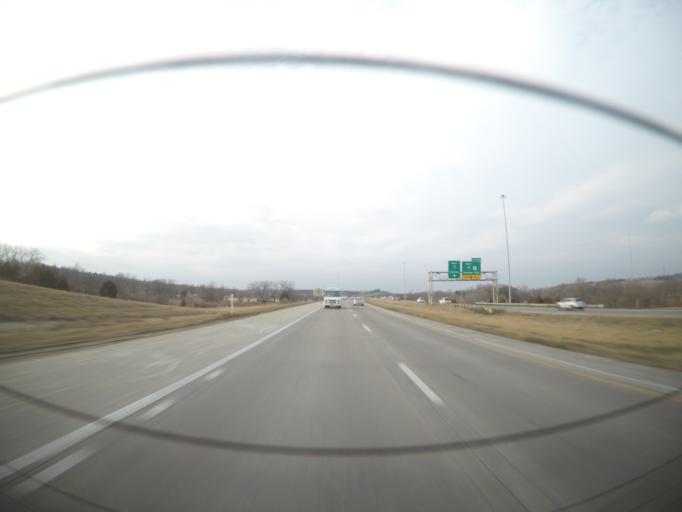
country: US
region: Kansas
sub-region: Shawnee County
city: Topeka
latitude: 39.0465
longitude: -95.7688
